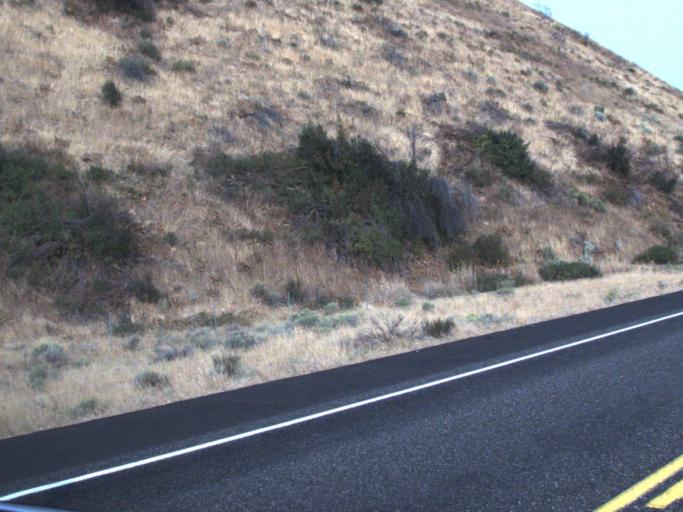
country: US
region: Washington
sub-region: Kittitas County
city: Ellensburg
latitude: 47.0886
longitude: -120.6513
